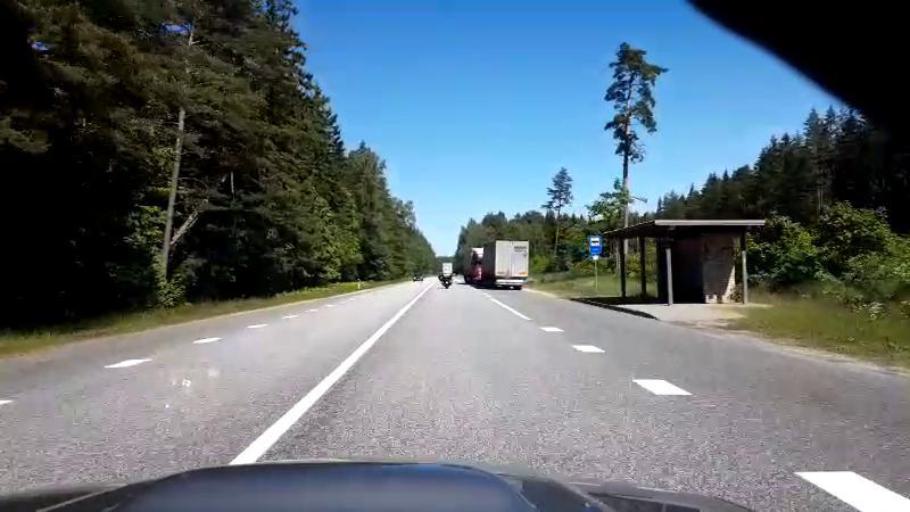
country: LV
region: Saulkrastu
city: Saulkrasti
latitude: 57.3927
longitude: 24.4286
